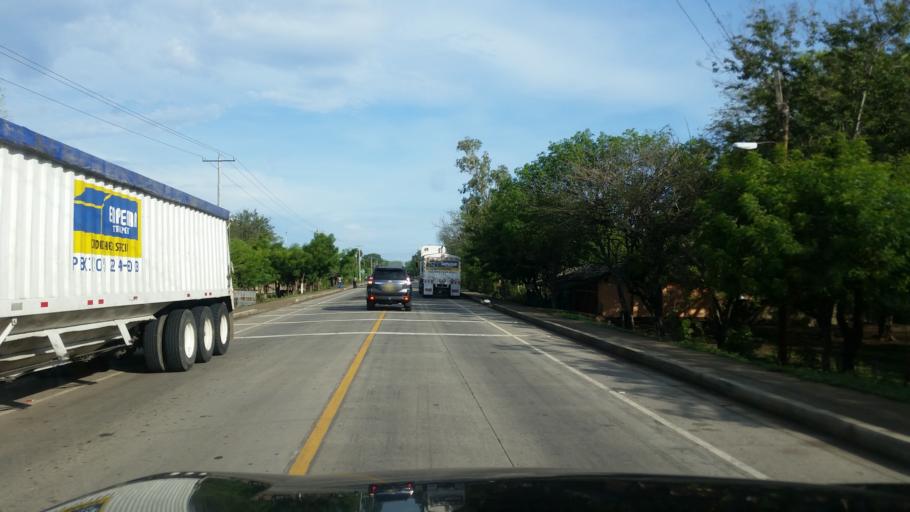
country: NI
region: Managua
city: Carlos Fonseca Amador
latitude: 12.1060
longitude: -86.5859
